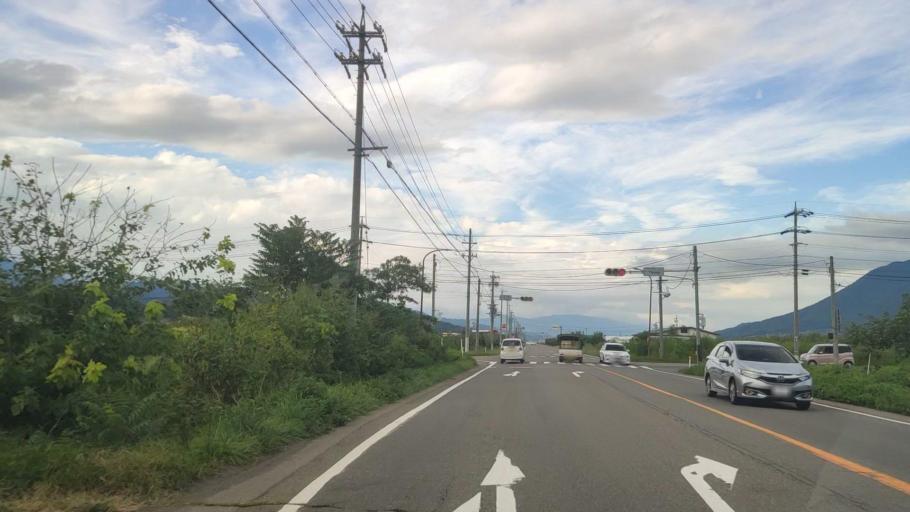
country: JP
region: Nagano
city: Nakano
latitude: 36.7665
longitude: 138.3504
